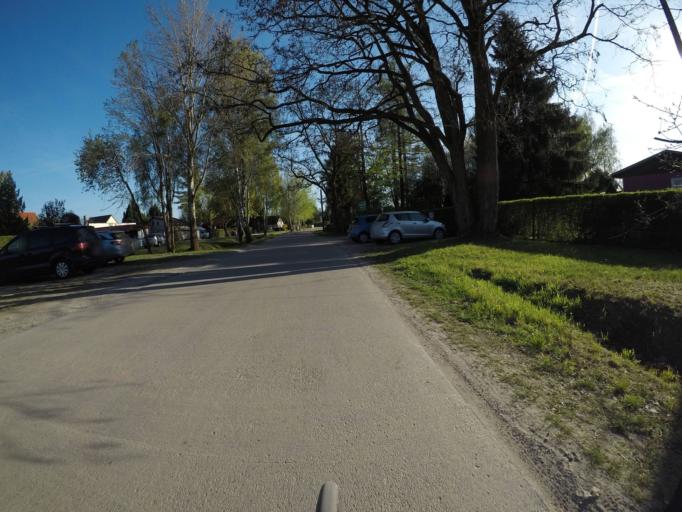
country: DE
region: Brandenburg
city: Neuenhagen
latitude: 52.5132
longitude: 13.7233
